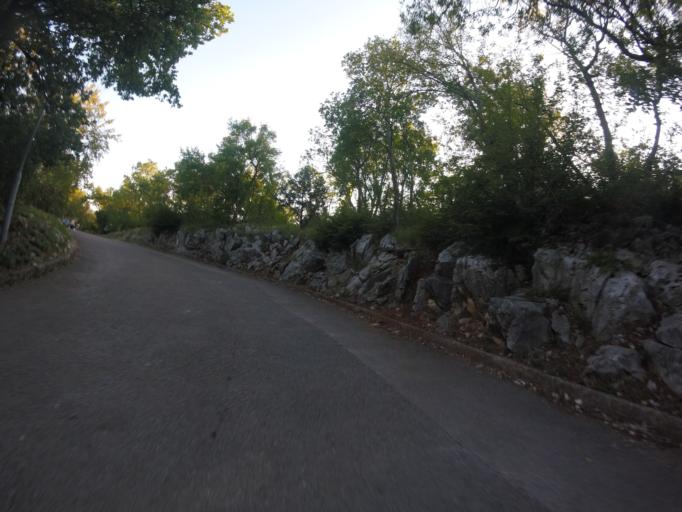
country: HR
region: Primorsko-Goranska
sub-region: Grad Crikvenica
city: Jadranovo
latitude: 45.2043
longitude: 14.6507
